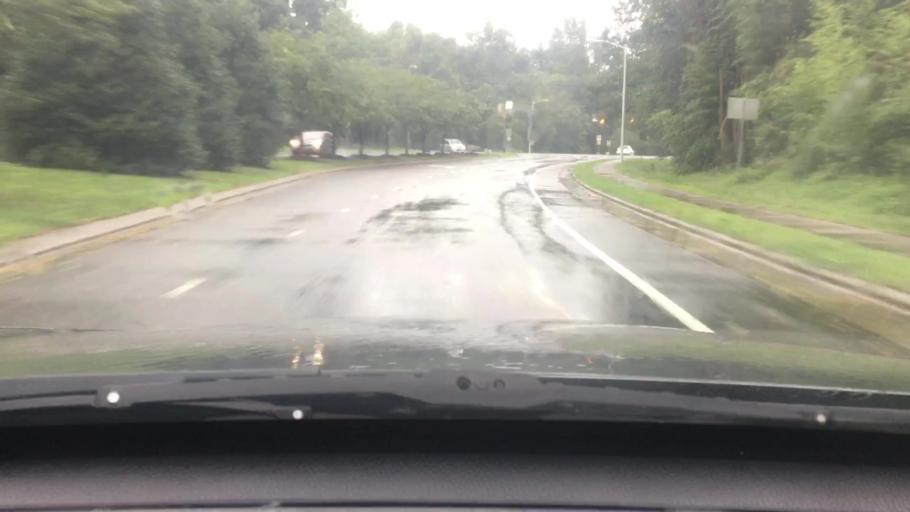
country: US
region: North Carolina
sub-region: Alamance County
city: Glen Raven
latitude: 36.0900
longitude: -79.4668
